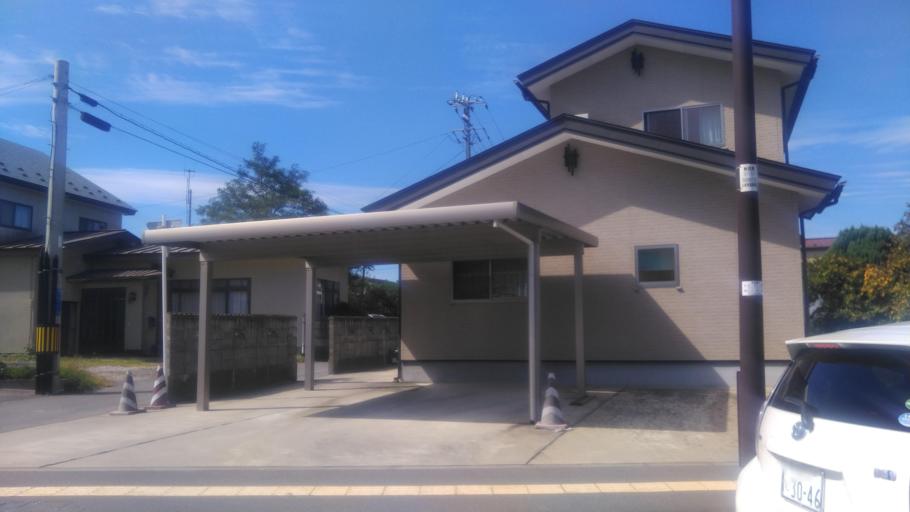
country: JP
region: Akita
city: Noshiromachi
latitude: 40.2015
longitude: 140.0225
